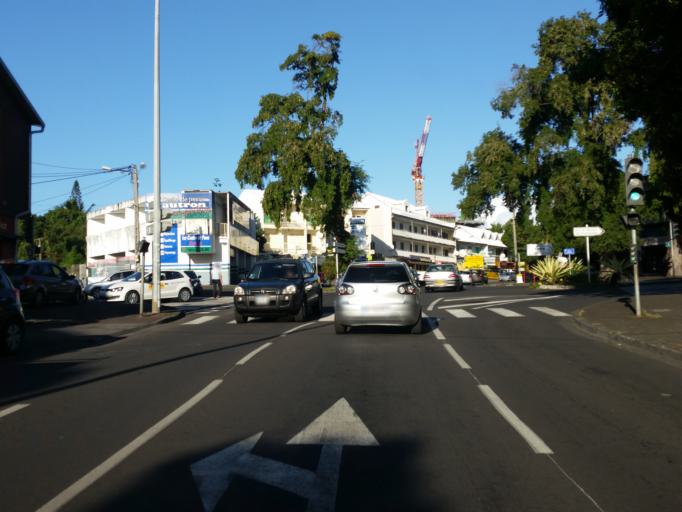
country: RE
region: Reunion
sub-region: Reunion
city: Saint-Denis
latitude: -20.8962
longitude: 55.4916
